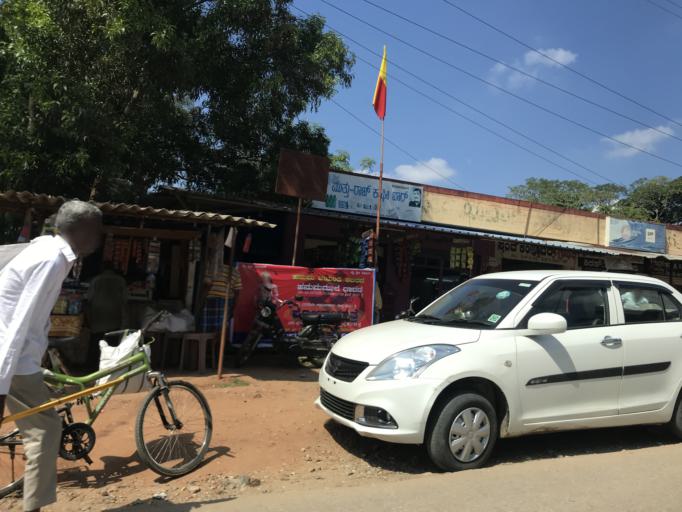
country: IN
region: Karnataka
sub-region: Mysore
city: Heggadadevankote
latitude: 12.0906
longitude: 76.3321
